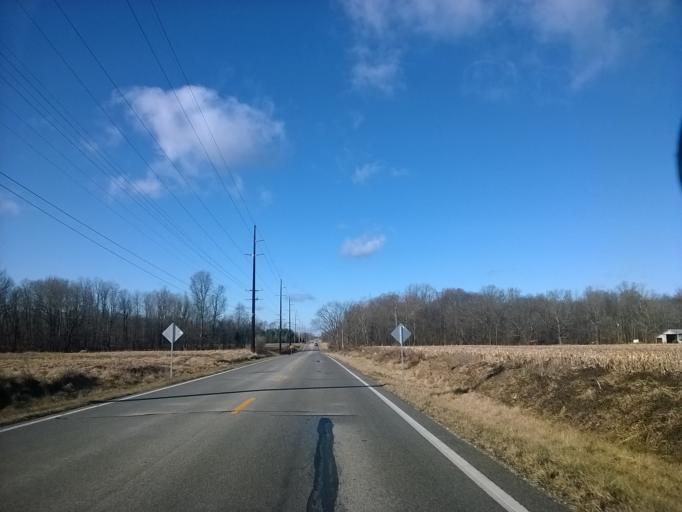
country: US
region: Indiana
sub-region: Scott County
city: Scottsburg
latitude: 38.7369
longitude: -85.6593
